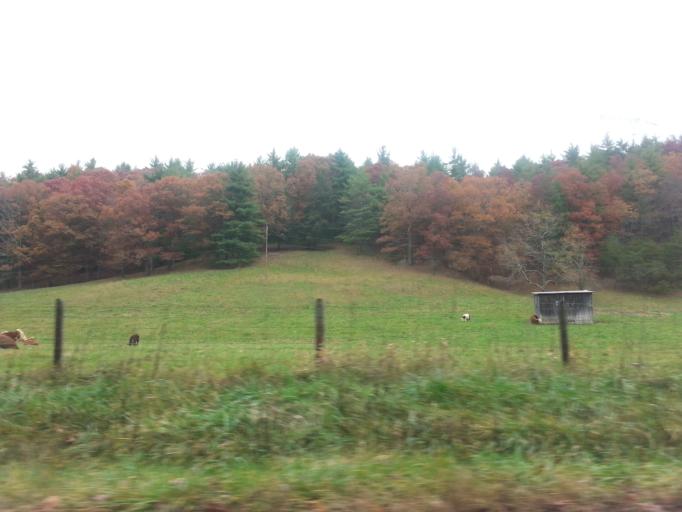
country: US
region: Virginia
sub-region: Bland County
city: Bland
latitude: 37.0692
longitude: -80.9707
